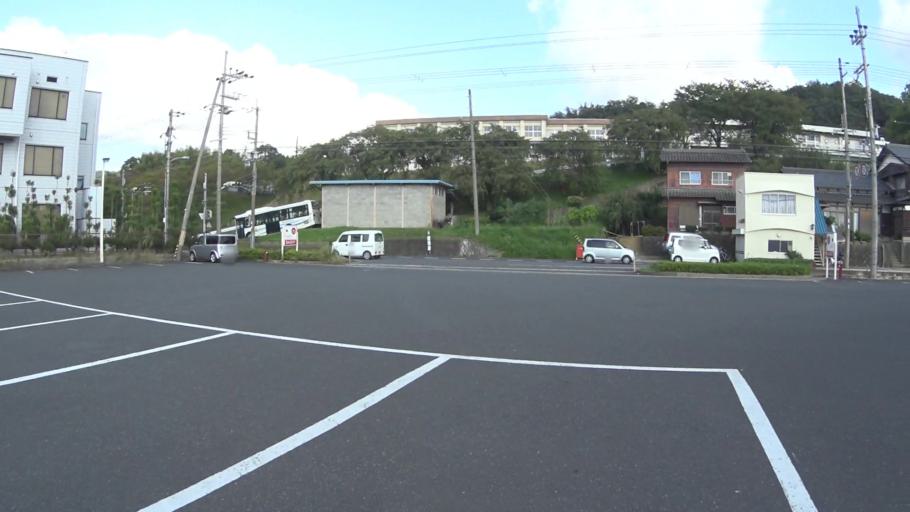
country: JP
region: Kyoto
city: Miyazu
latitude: 35.5737
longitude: 135.1705
